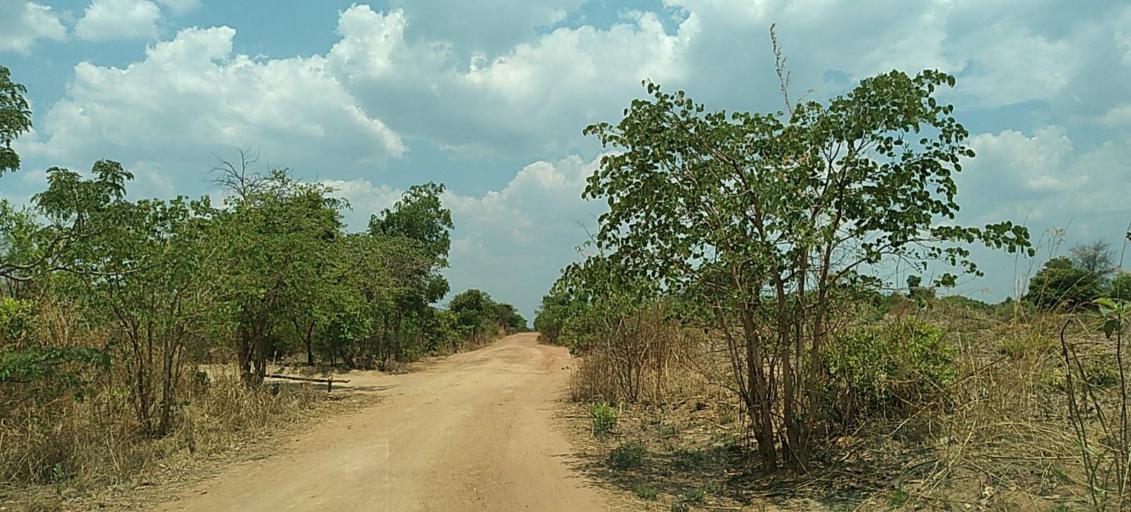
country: ZM
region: Copperbelt
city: Luanshya
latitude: -13.3807
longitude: 28.4351
